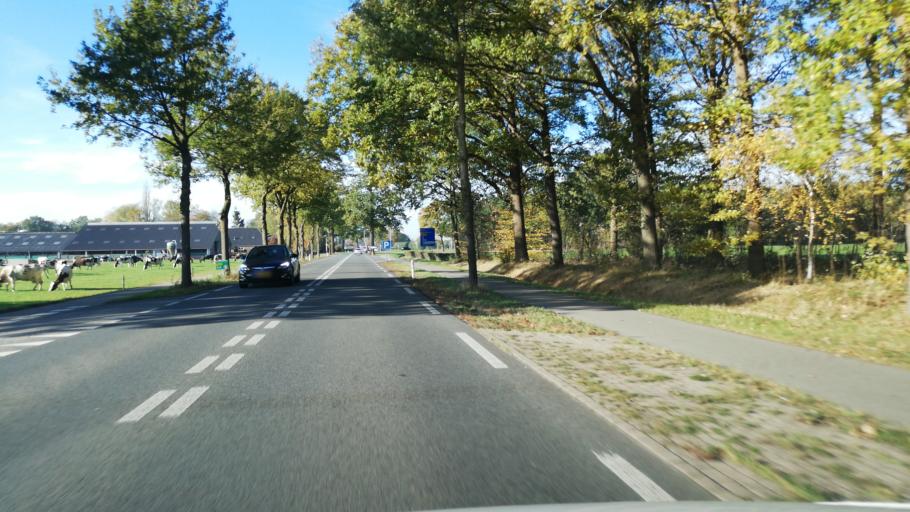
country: NL
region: Gelderland
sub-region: Gemeente Voorst
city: Twello
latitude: 52.1882
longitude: 6.0953
